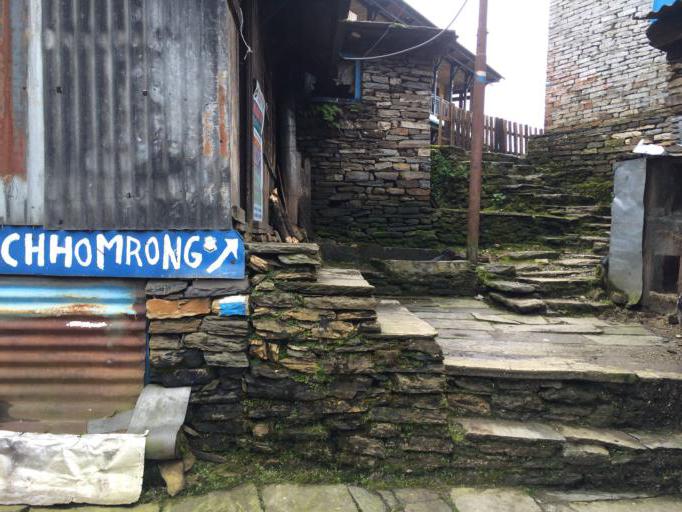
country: NP
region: Western Region
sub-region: Dhawalagiri Zone
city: Chitre
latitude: 28.3963
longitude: 83.7653
